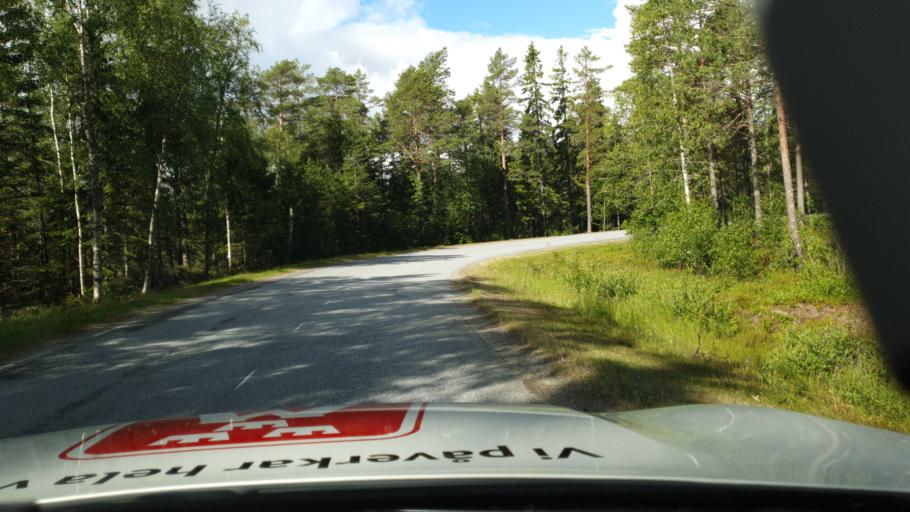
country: SE
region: Vaesterbotten
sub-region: Umea Kommun
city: Roback
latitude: 63.6759
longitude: 20.0886
